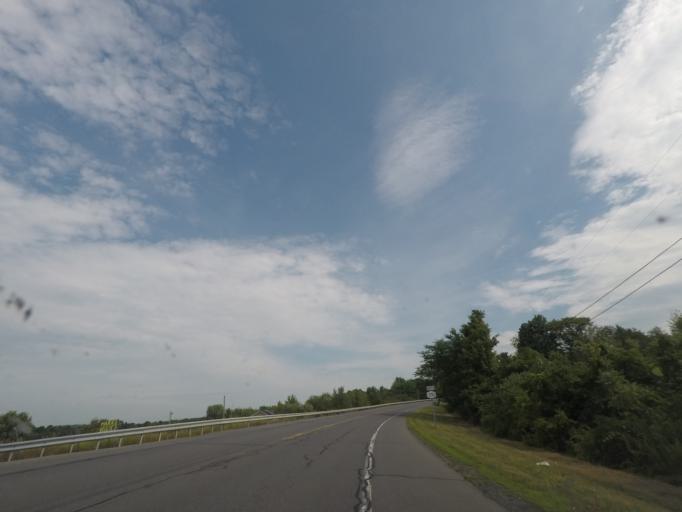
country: US
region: New York
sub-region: Rensselaer County
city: Poestenkill
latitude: 42.7060
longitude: -73.5628
